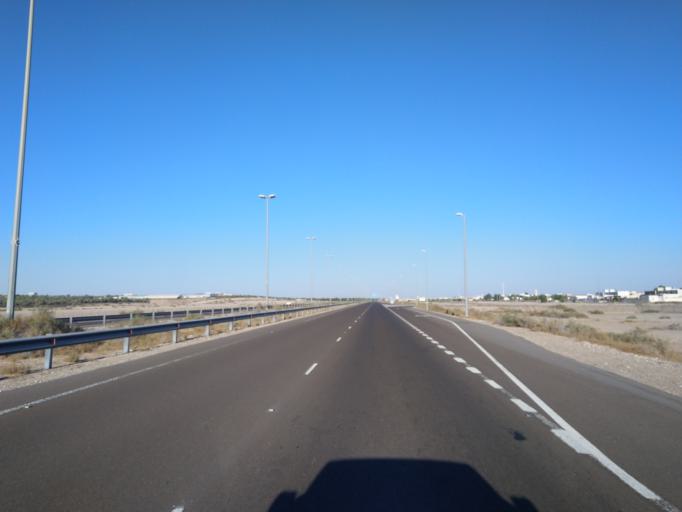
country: OM
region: Al Buraimi
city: Al Buraymi
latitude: 24.5074
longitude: 55.4670
